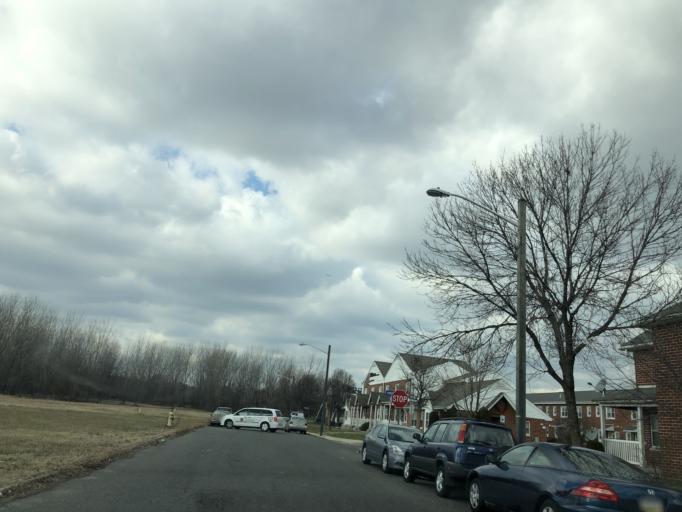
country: US
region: New Jersey
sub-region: Camden County
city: Wood-Lynne
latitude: 39.9405
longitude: -75.0929
